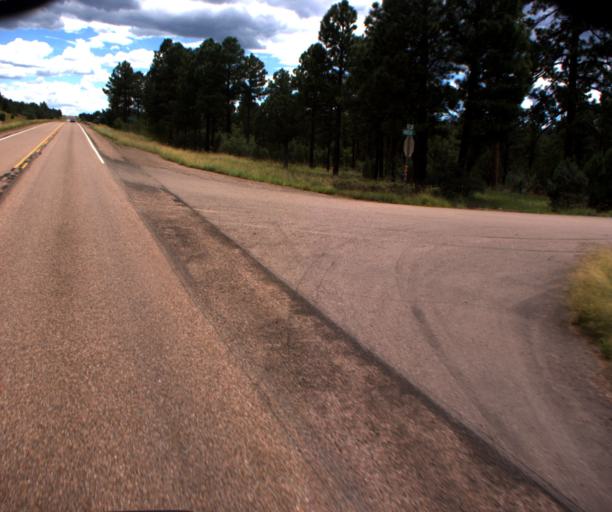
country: US
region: Arizona
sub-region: Navajo County
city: Linden
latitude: 34.3017
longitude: -110.1993
